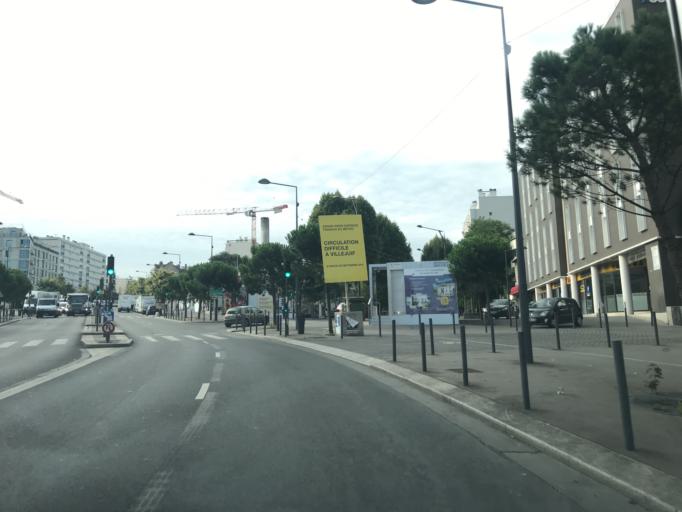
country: FR
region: Ile-de-France
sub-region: Departement du Val-de-Marne
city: Villejuif
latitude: 48.8000
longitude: 2.3653
